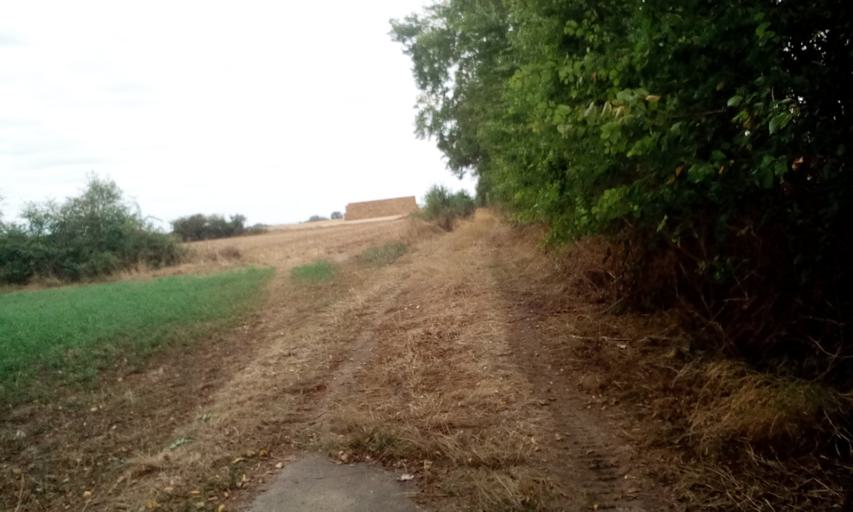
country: FR
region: Lower Normandy
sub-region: Departement du Calvados
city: Fontaine-Etoupefour
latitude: 49.1354
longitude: -0.4640
